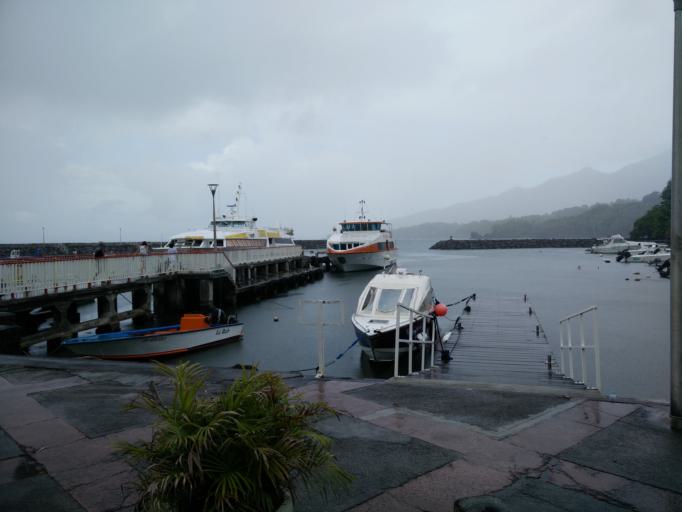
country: GP
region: Guadeloupe
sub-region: Guadeloupe
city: Trois-Rivieres
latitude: 15.9685
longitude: -61.6444
